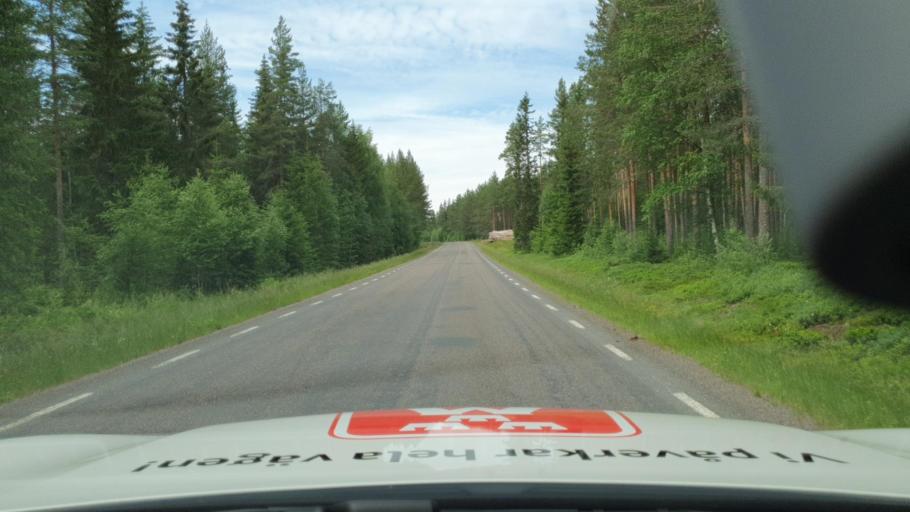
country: NO
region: Hedmark
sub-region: Grue
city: Kirkenaer
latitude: 60.6960
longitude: 12.6228
